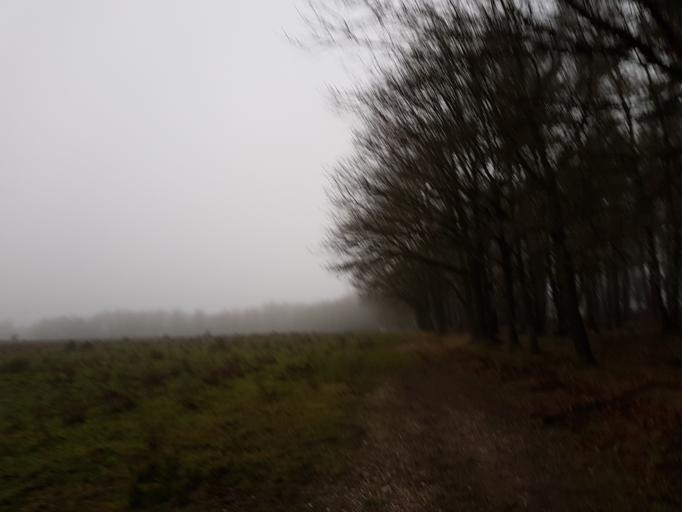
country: NL
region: Gelderland
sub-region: Gemeente Apeldoorn
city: Loenen
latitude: 52.0812
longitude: 5.9561
